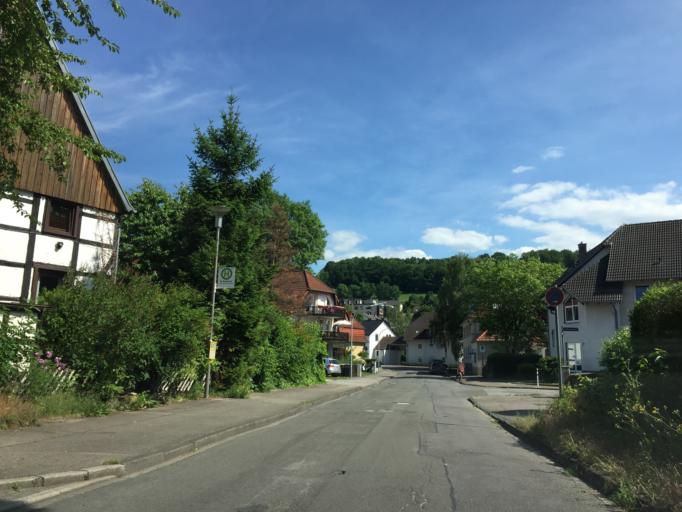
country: DE
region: North Rhine-Westphalia
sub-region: Regierungsbezirk Arnsberg
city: Nachrodt-Wiblingwerde
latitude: 51.3721
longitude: 7.6302
